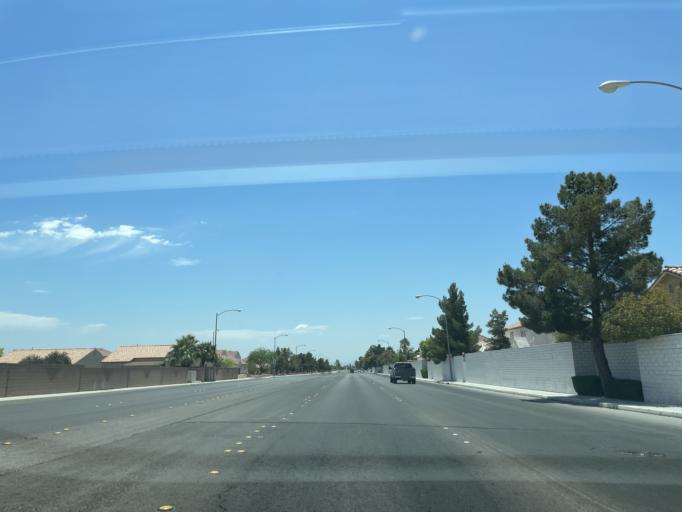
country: US
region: Nevada
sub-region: Clark County
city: North Las Vegas
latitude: 36.2739
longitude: -115.1532
